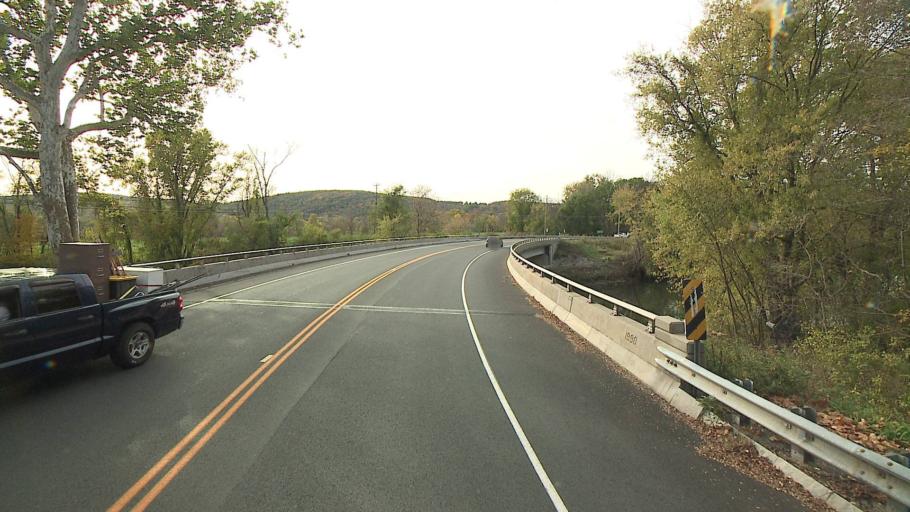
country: US
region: Connecticut
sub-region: Litchfield County
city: Canaan
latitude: 42.0051
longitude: -73.3568
